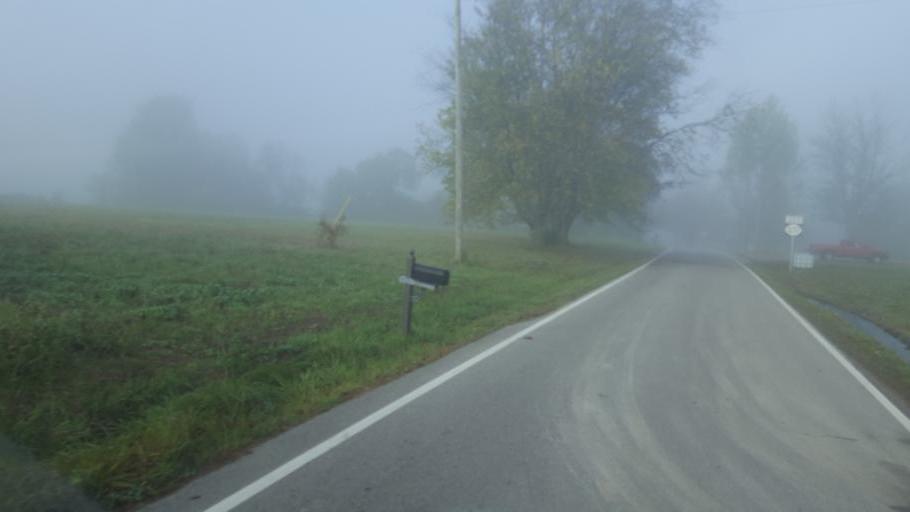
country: US
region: Kentucky
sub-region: Fleming County
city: Flemingsburg
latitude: 38.4959
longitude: -83.5707
